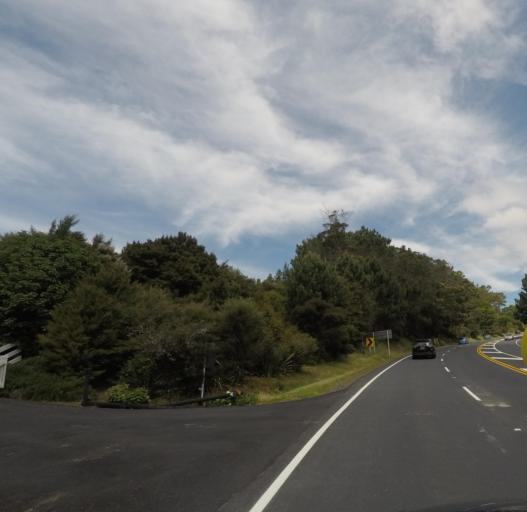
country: NZ
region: Auckland
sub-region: Auckland
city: Rothesay Bay
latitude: -36.6862
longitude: 174.7055
